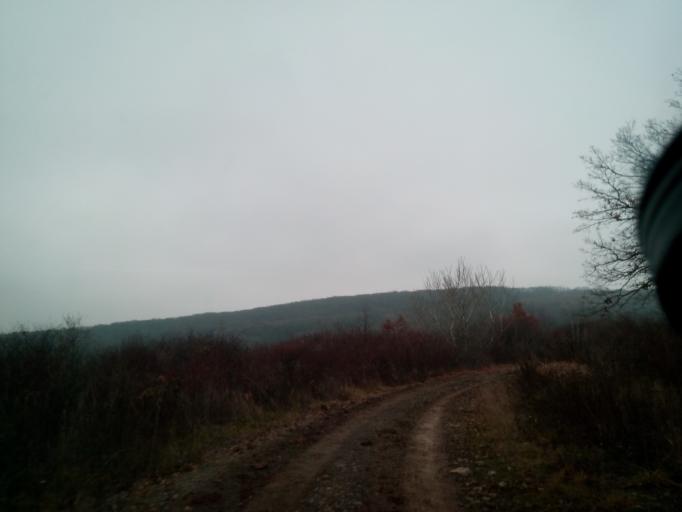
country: SK
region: Kosicky
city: Kosice
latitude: 48.6916
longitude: 21.4469
